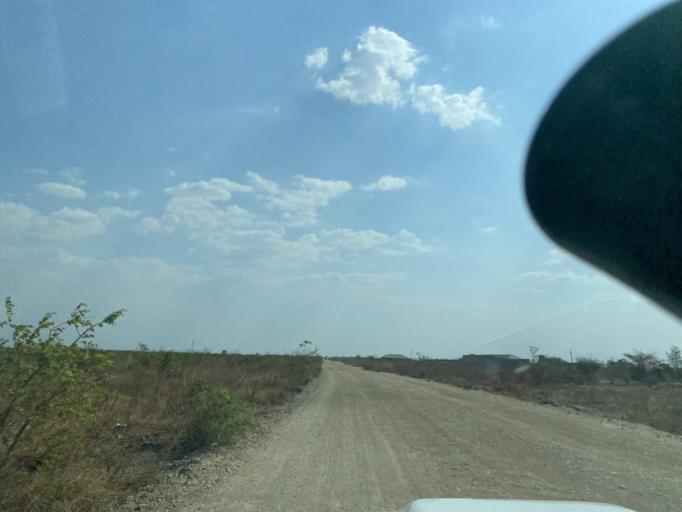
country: ZM
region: Lusaka
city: Lusaka
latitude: -15.3587
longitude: 28.0963
